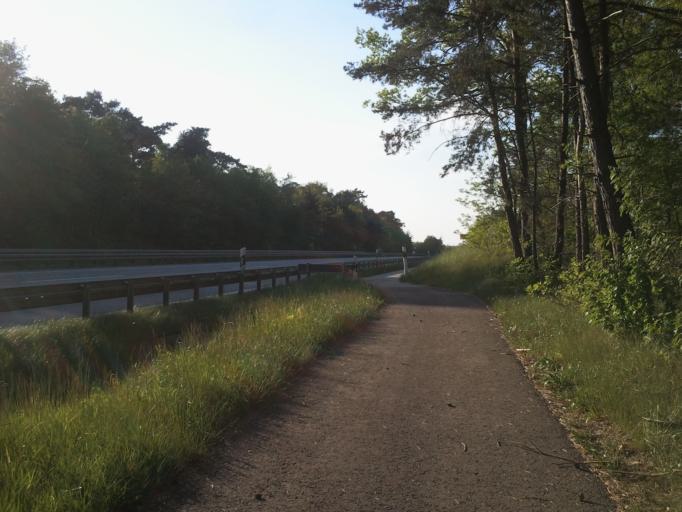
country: DE
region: Lower Saxony
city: Nienburg
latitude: 52.6150
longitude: 9.2498
